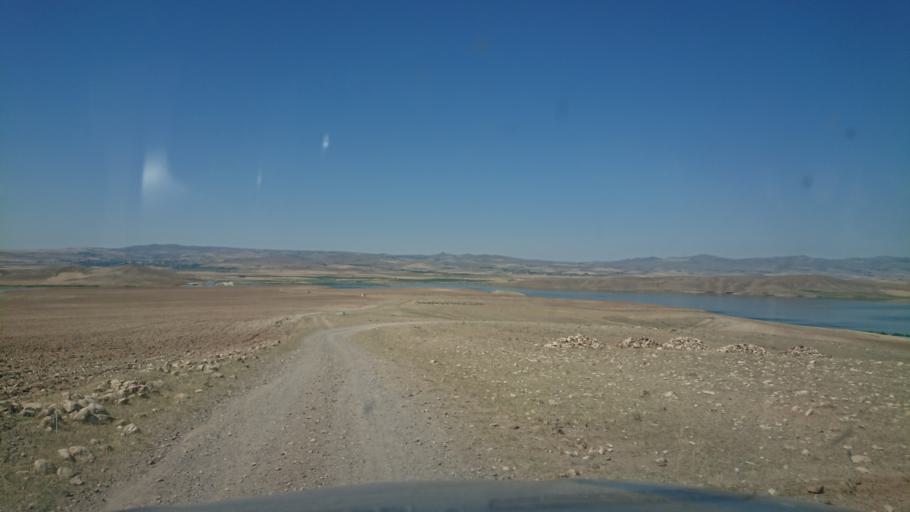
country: TR
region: Aksaray
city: Sariyahsi
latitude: 39.0543
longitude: 33.8865
